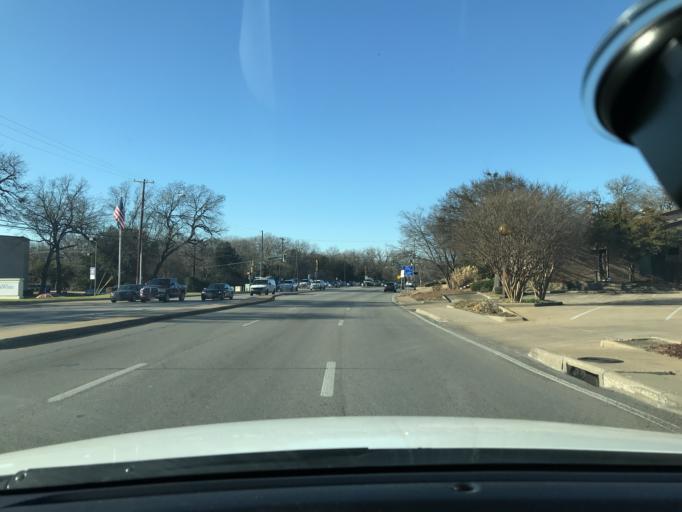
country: US
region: Texas
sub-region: Dallas County
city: Highland Park
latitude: 32.8349
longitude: -96.7036
